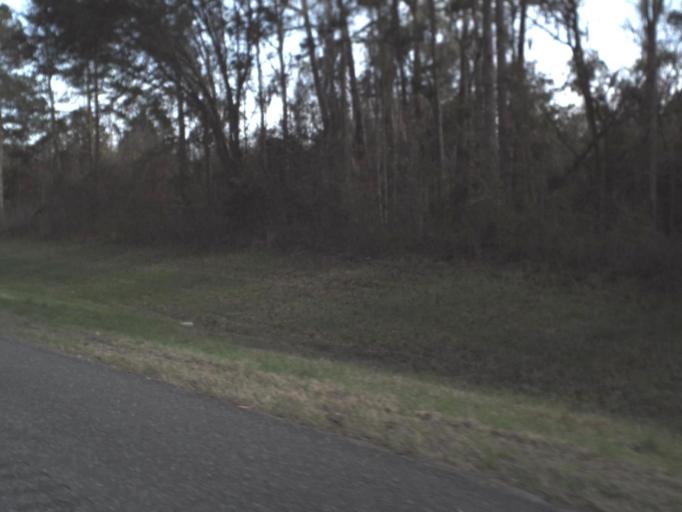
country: US
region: Florida
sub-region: Leon County
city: Tallahassee
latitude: 30.4781
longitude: -84.1346
